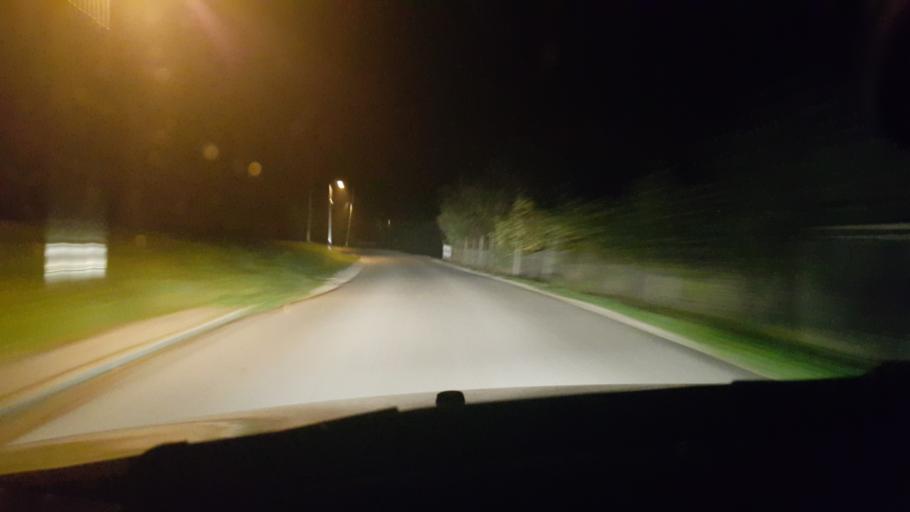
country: SI
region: Slovenska Bistrica
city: Pragersko
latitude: 46.3671
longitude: 15.6295
